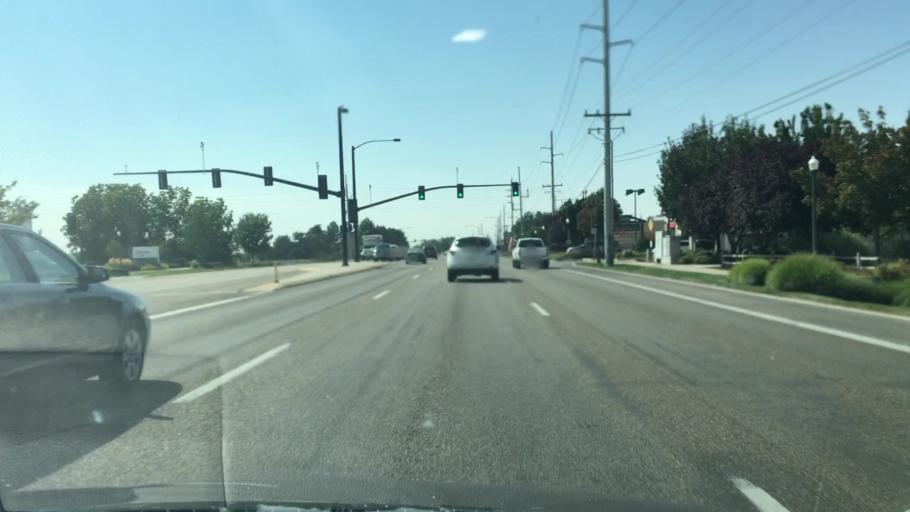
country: US
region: Idaho
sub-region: Ada County
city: Eagle
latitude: 43.6833
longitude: -116.3161
